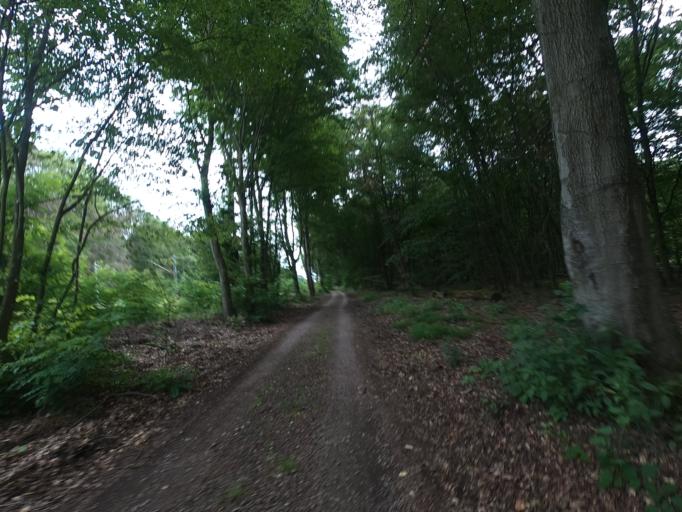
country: DE
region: Hesse
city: Langen
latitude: 50.0122
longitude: 8.6593
